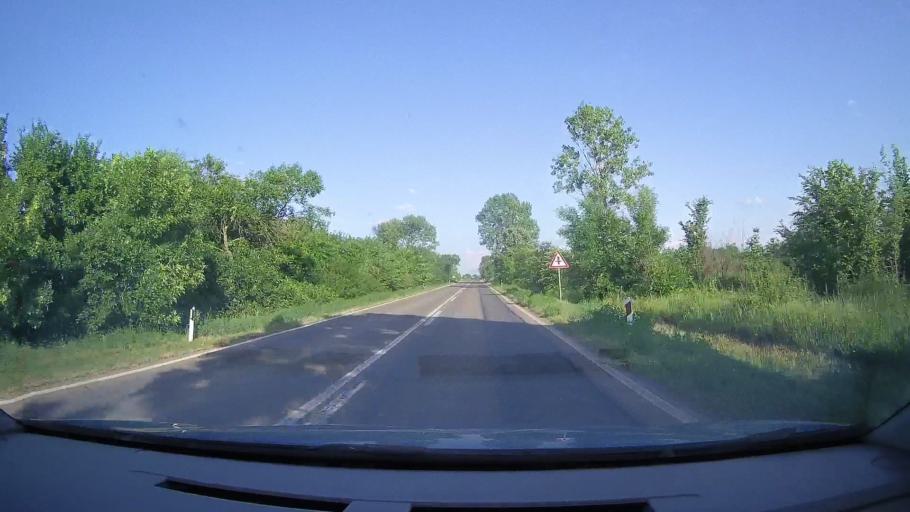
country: RS
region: Autonomna Pokrajina Vojvodina
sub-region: Juznobanatski Okrug
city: Alibunar
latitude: 45.0665
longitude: 20.9719
